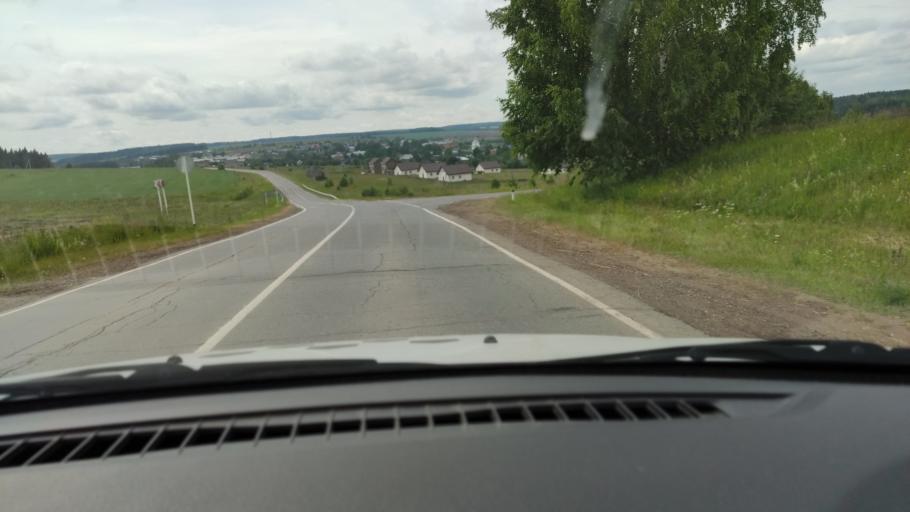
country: RU
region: Perm
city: Kukushtan
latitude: 57.4675
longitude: 56.5535
